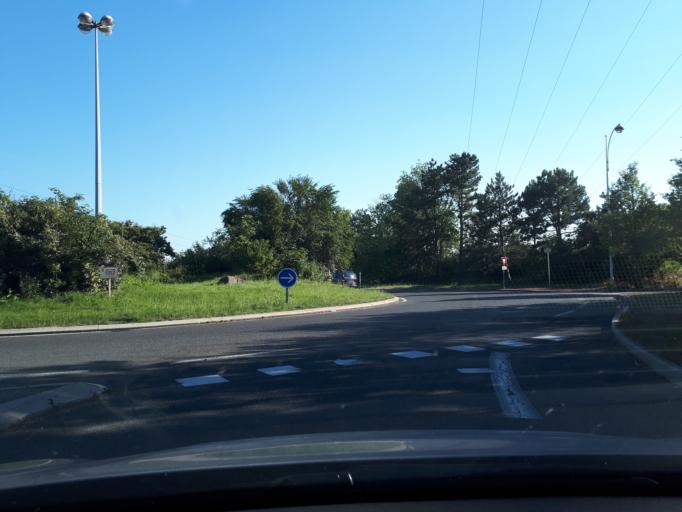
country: FR
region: Rhone-Alpes
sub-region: Departement du Rhone
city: Saint-Bonnet-de-Mure
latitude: 45.7273
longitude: 5.0293
